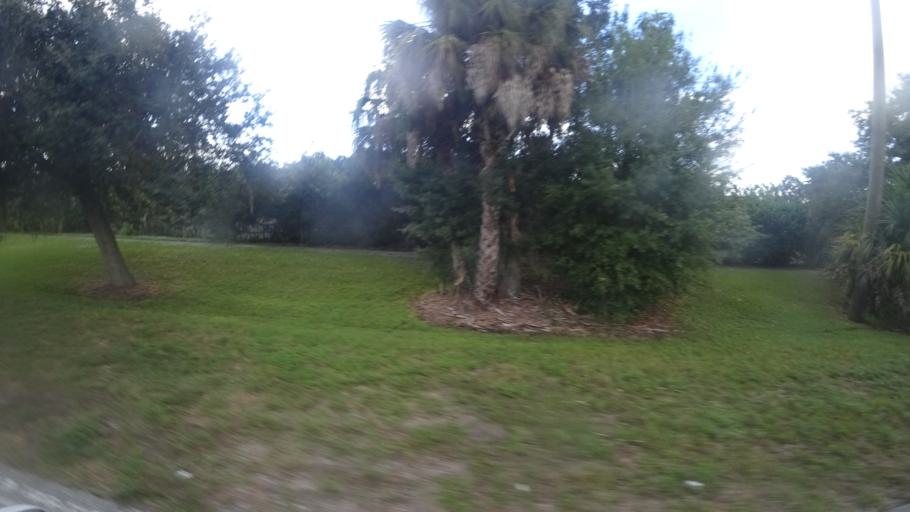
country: US
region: Florida
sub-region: Manatee County
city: Memphis
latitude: 27.6189
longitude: -82.5274
